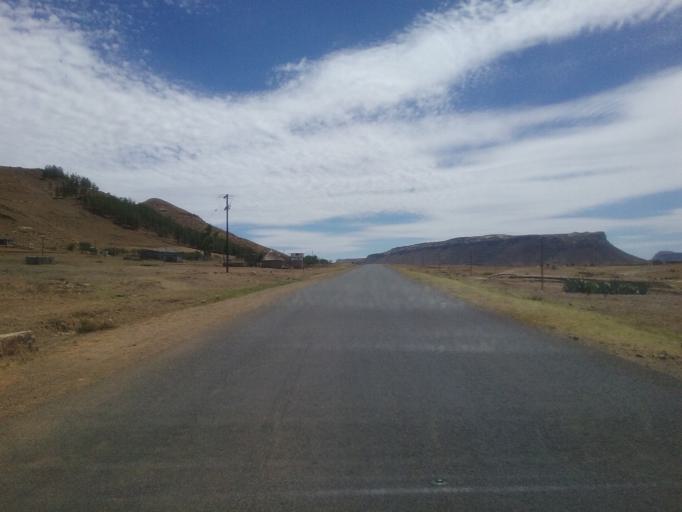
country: LS
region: Mafeteng
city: Mafeteng
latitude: -29.9169
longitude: 27.2484
